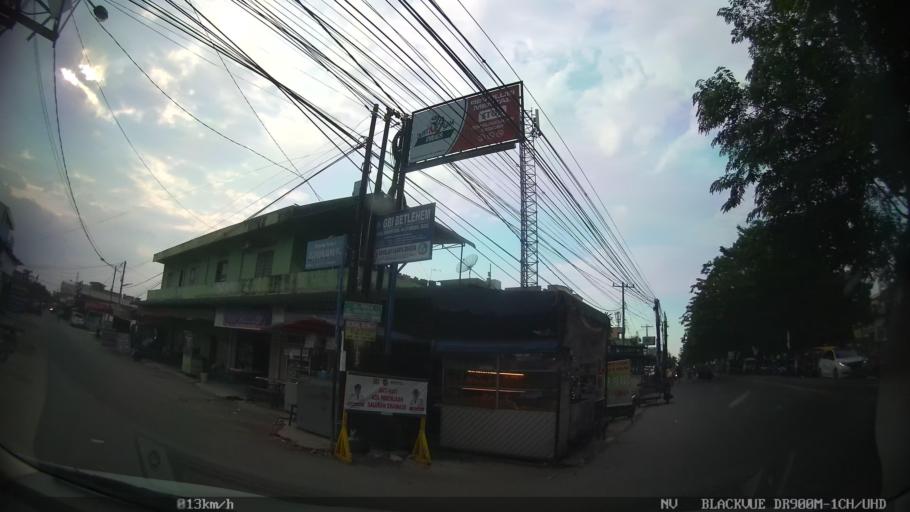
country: ID
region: North Sumatra
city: Medan
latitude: 3.6066
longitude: 98.7069
